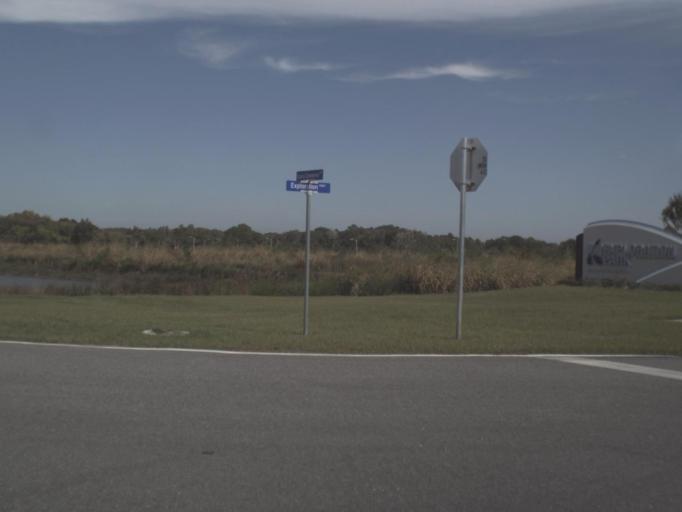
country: US
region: Florida
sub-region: Brevard County
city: Merritt Island
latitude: 28.5114
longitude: -80.6756
